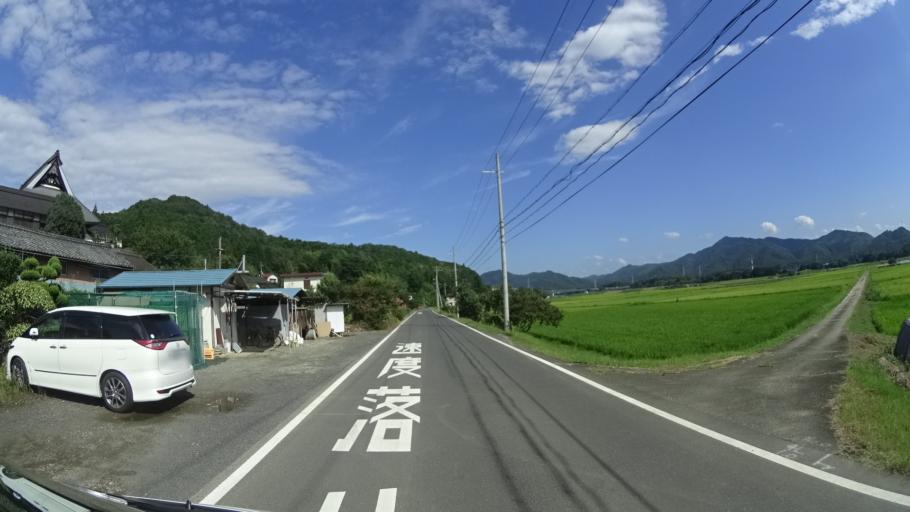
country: JP
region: Kyoto
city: Ayabe
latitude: 35.3177
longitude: 135.1859
